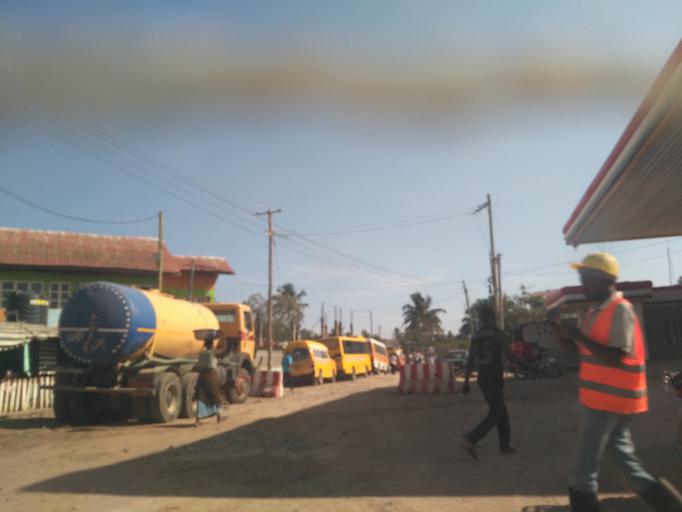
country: TZ
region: Mwanza
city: Mwanza
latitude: -2.5061
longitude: 32.8983
